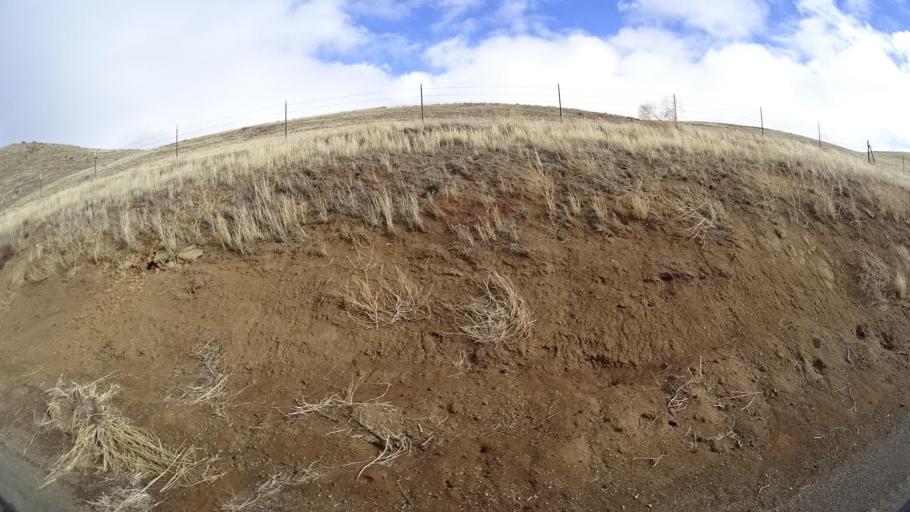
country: US
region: California
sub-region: Kern County
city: Maricopa
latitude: 34.9104
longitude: -119.3945
